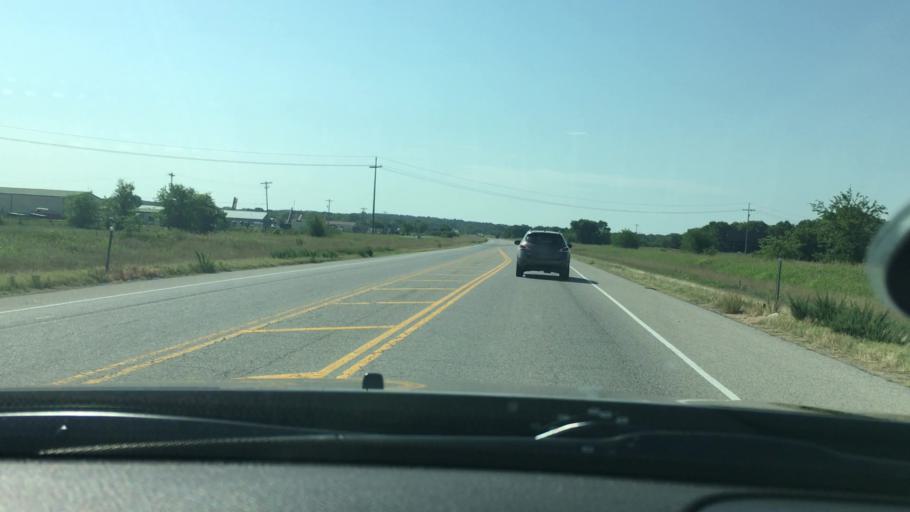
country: US
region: Oklahoma
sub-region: Pontotoc County
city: Ada
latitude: 34.7121
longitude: -96.6187
